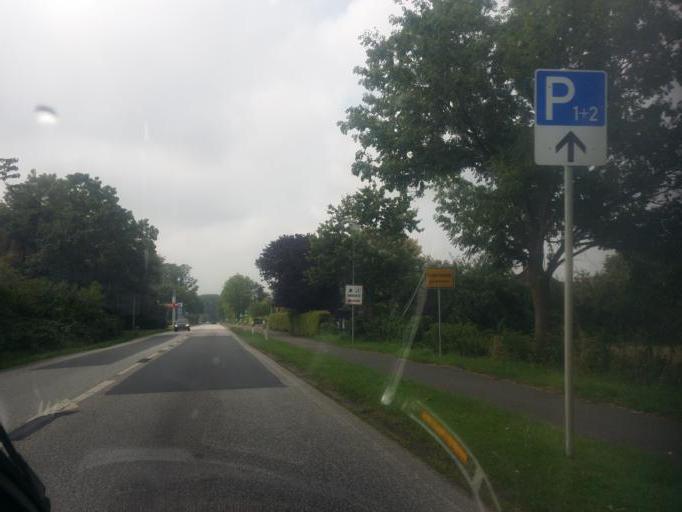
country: DE
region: Schleswig-Holstein
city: Friedrichstadt
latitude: 54.3720
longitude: 9.0937
